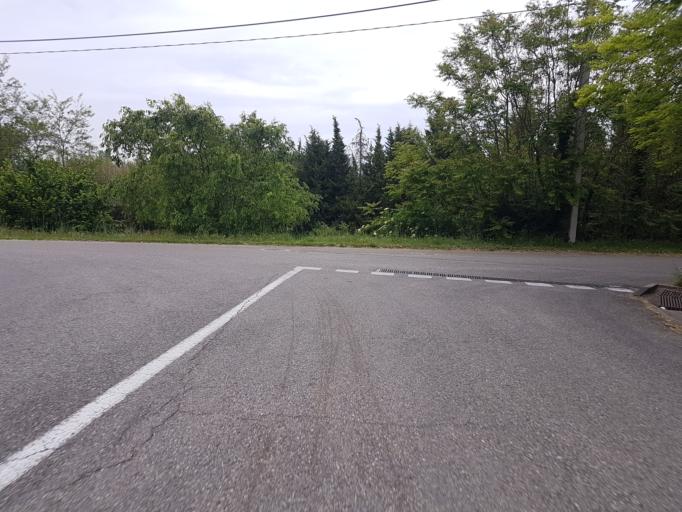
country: FR
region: Provence-Alpes-Cote d'Azur
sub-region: Departement du Vaucluse
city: Mondragon
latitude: 44.2440
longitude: 4.7264
